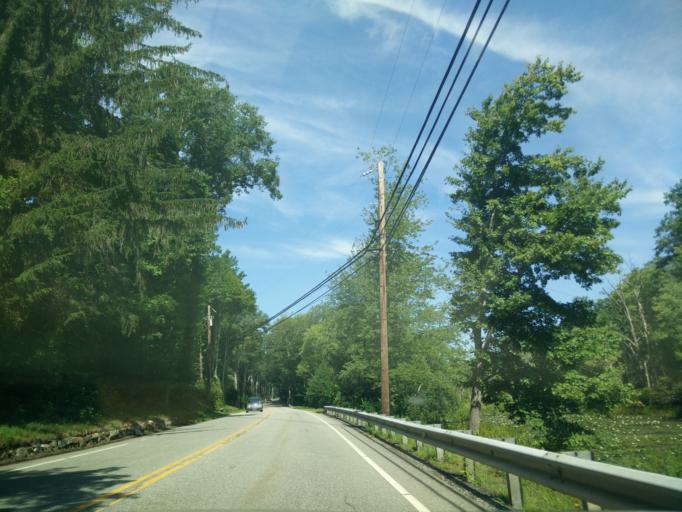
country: US
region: Connecticut
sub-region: Middlesex County
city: Clinton
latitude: 41.3415
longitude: -72.5560
